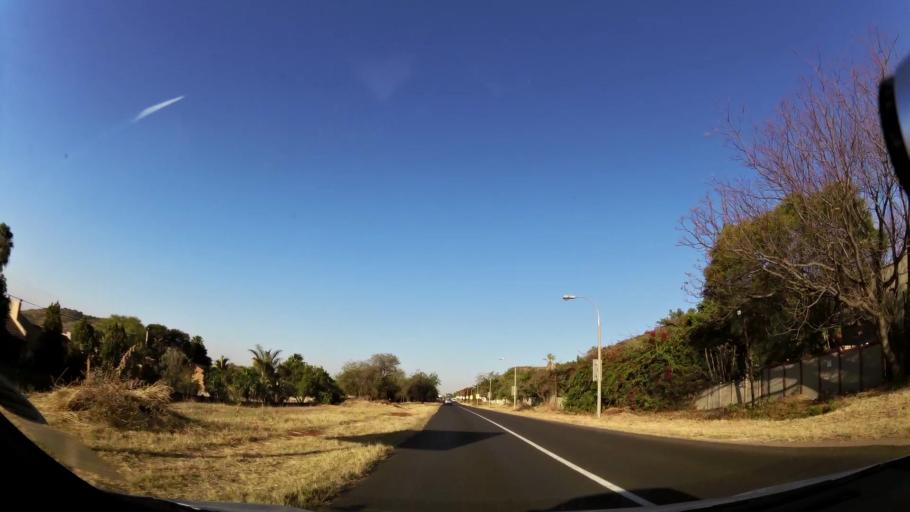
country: ZA
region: North-West
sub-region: Bojanala Platinum District Municipality
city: Rustenburg
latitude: -25.7015
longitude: 27.2216
